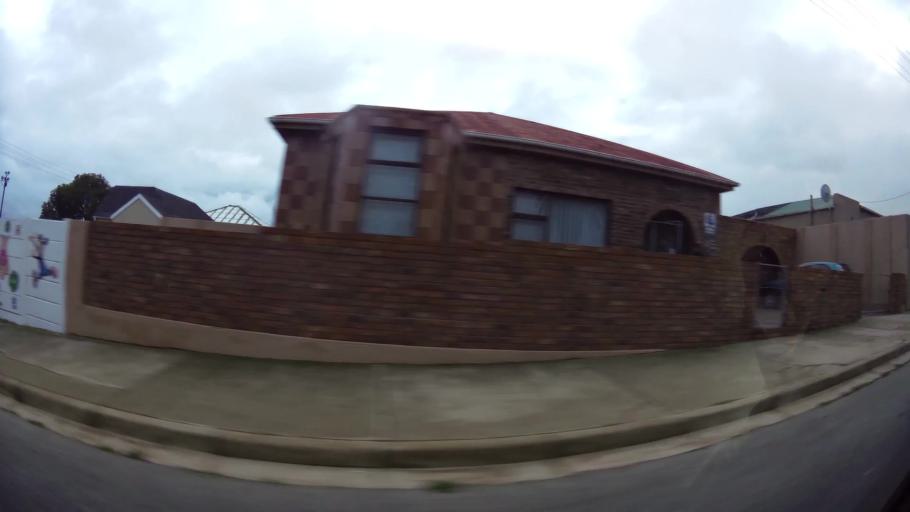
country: ZA
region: Eastern Cape
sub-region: Nelson Mandela Bay Metropolitan Municipality
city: Port Elizabeth
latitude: -33.9296
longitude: 25.5966
